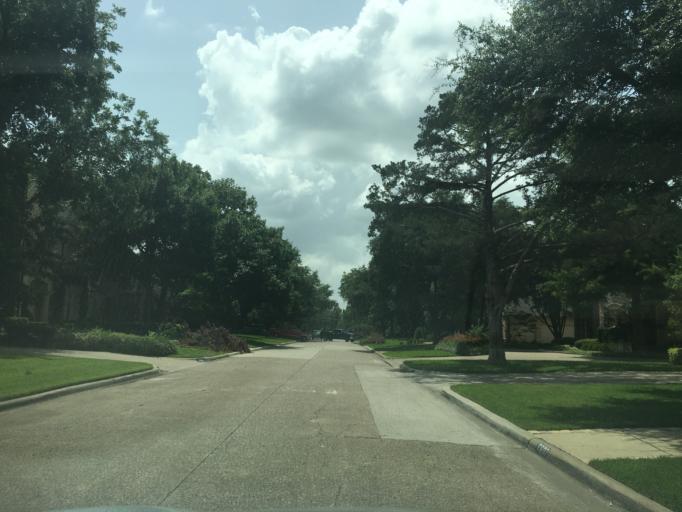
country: US
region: Texas
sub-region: Dallas County
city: University Park
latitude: 32.8894
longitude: -96.7912
